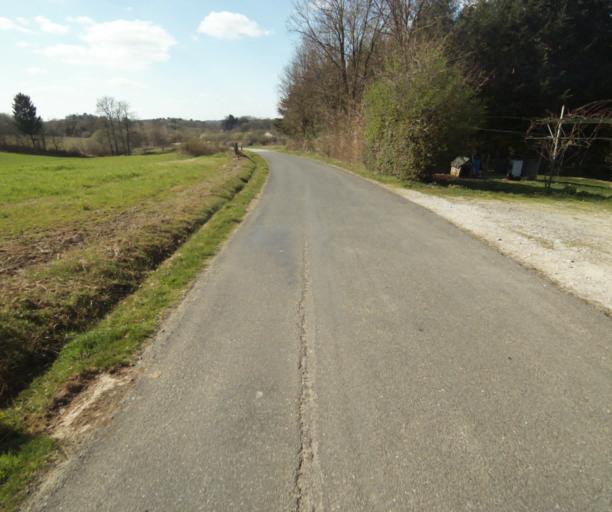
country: FR
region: Limousin
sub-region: Departement de la Correze
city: Saint-Mexant
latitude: 45.3028
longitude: 1.6601
